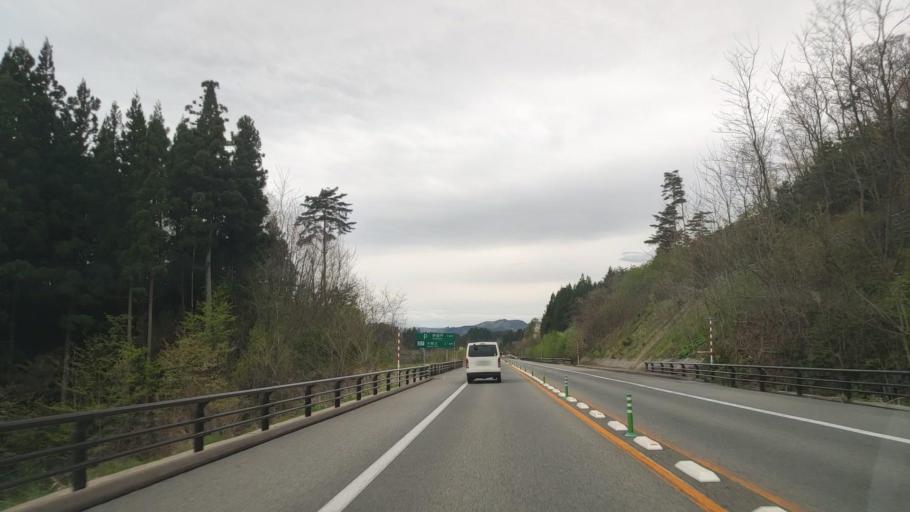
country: JP
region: Akita
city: Odate
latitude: 40.3181
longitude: 140.5876
